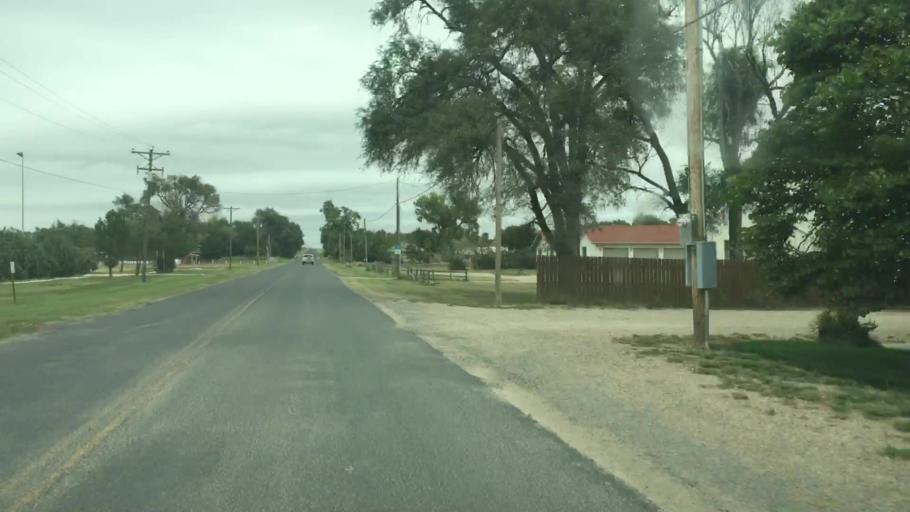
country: US
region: Kansas
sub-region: Hamilton County
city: Syracuse
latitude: 38.0545
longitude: -102.1186
